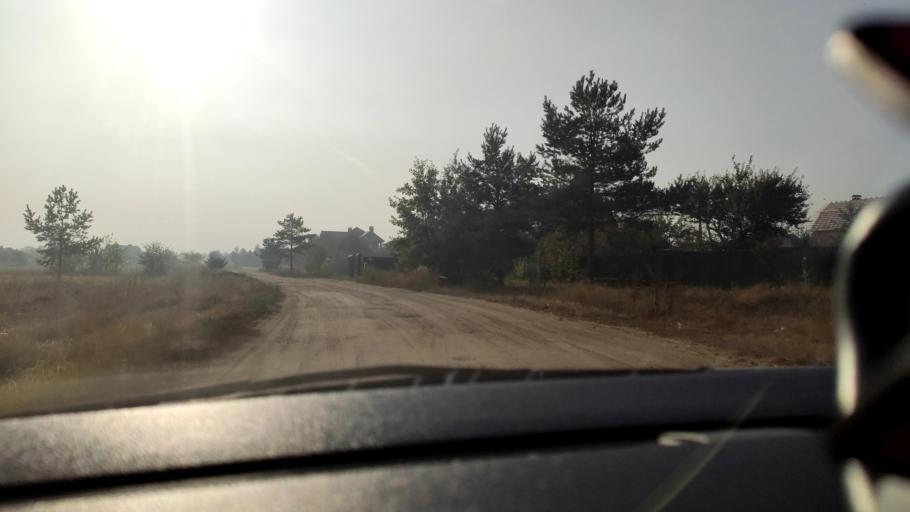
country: RU
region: Voronezj
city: Pridonskoy
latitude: 51.6354
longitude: 39.1059
